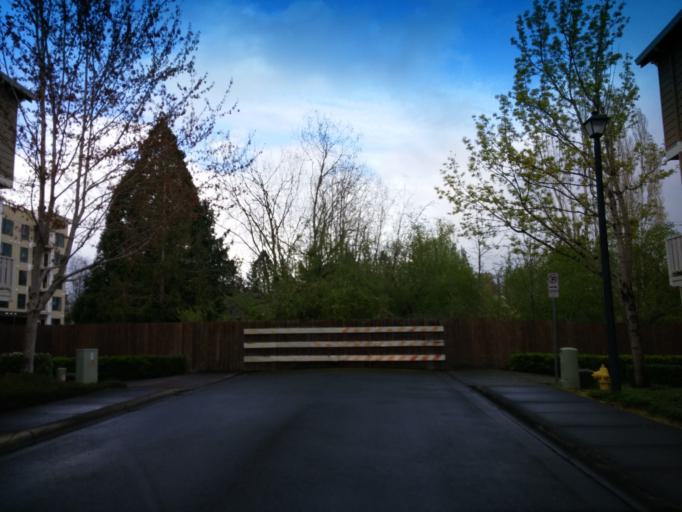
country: US
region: Oregon
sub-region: Washington County
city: Oak Hills
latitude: 45.5113
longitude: -122.8410
